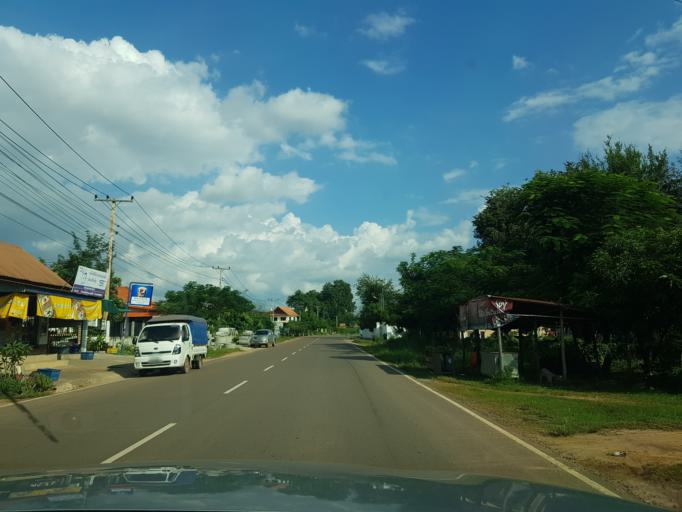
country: TH
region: Nong Khai
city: Pho Tak
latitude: 17.9786
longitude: 102.4644
